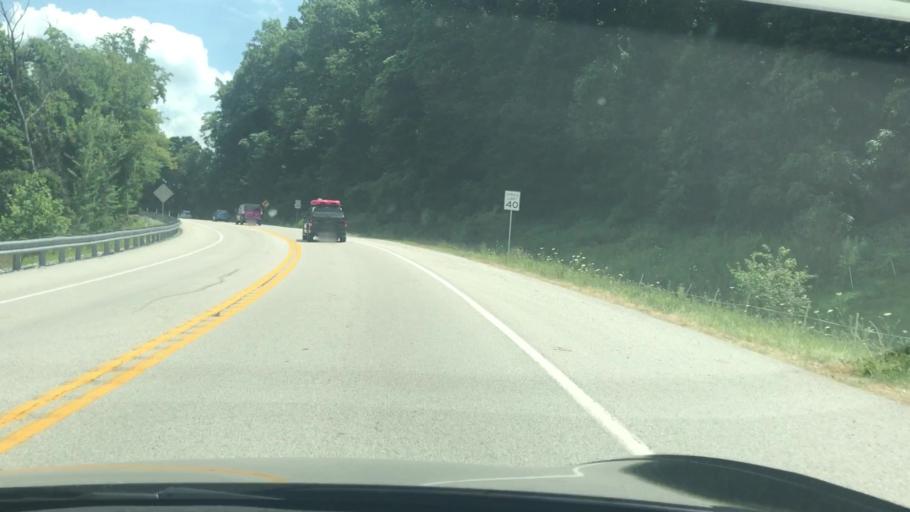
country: US
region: Pennsylvania
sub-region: York County
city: Manchester
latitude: 40.0990
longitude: -76.7630
